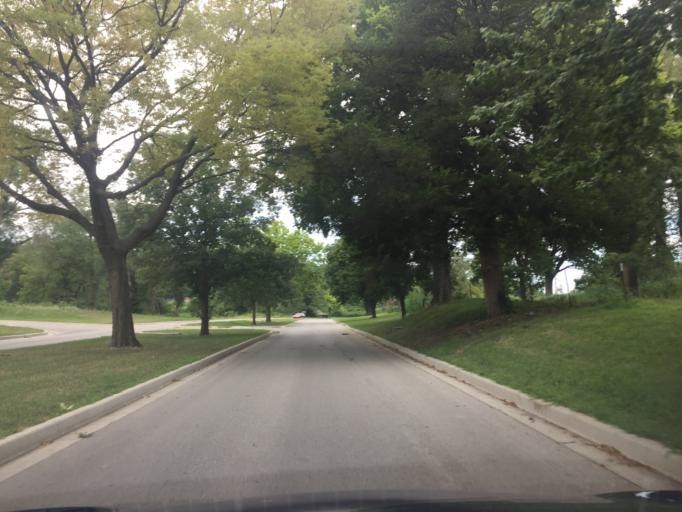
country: US
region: Missouri
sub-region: Platte County
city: Weston
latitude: 39.3631
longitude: -94.9187
